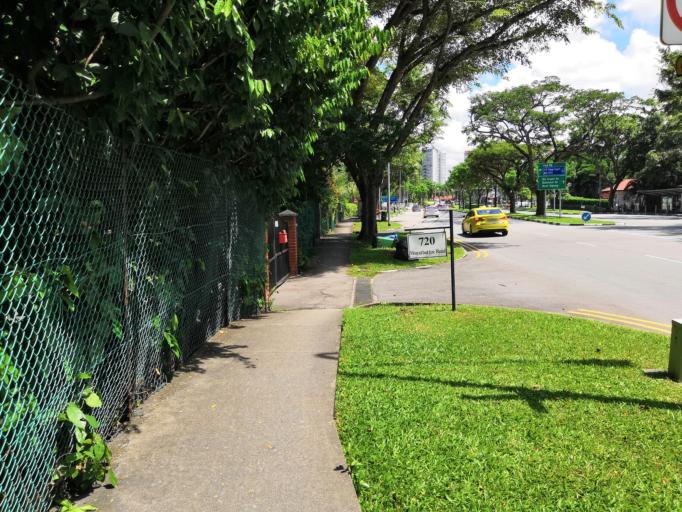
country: SG
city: Singapore
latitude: 1.3007
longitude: 103.8869
